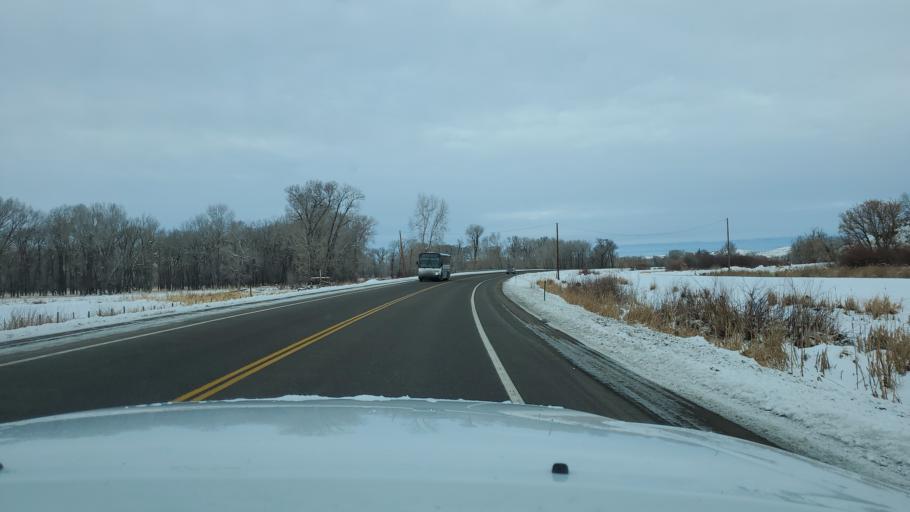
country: US
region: Colorado
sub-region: Routt County
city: Hayden
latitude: 40.4941
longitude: -107.3681
